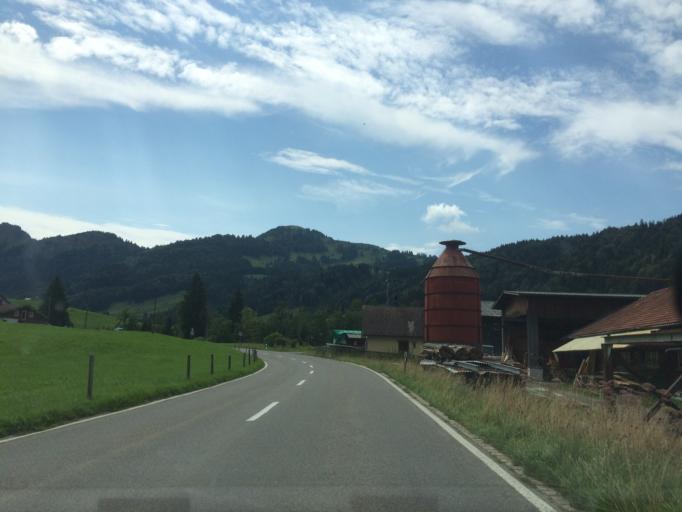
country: CH
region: Appenzell Ausserrhoden
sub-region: Bezirk Hinterland
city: Urnasch
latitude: 47.3027
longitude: 9.2738
